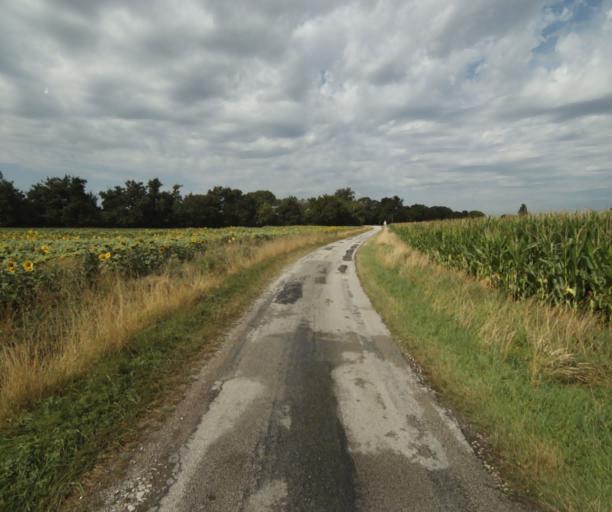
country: FR
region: Midi-Pyrenees
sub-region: Departement de la Haute-Garonne
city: Saint-Felix-Lauragais
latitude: 43.4309
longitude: 1.9476
